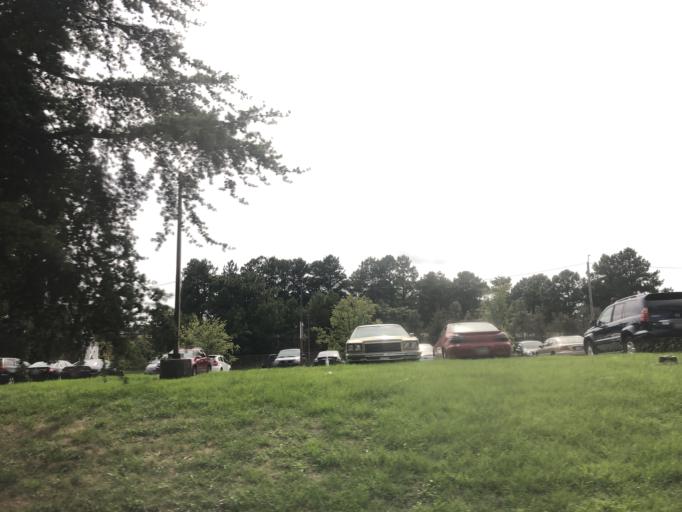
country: US
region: Georgia
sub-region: Fulton County
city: College Park
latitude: 33.6494
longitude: -84.4486
